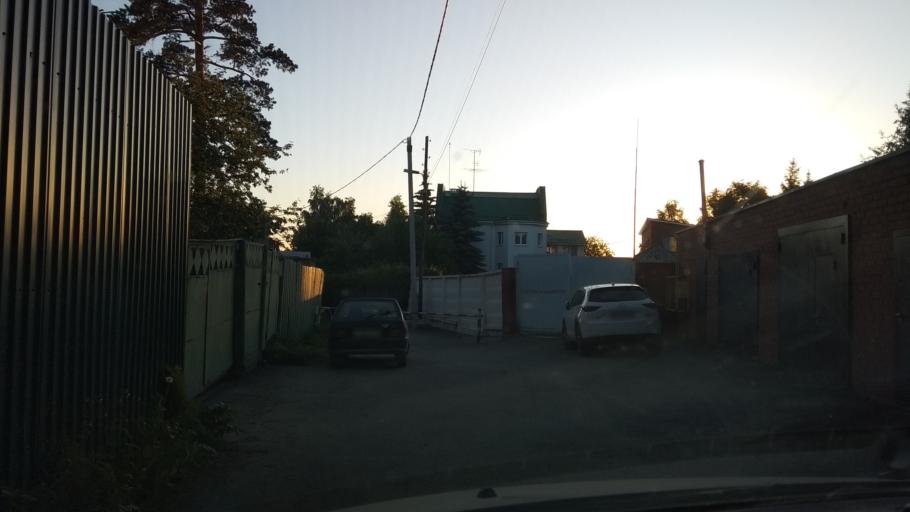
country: RU
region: Sverdlovsk
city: Sredneuralsk
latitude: 56.9916
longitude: 60.4570
